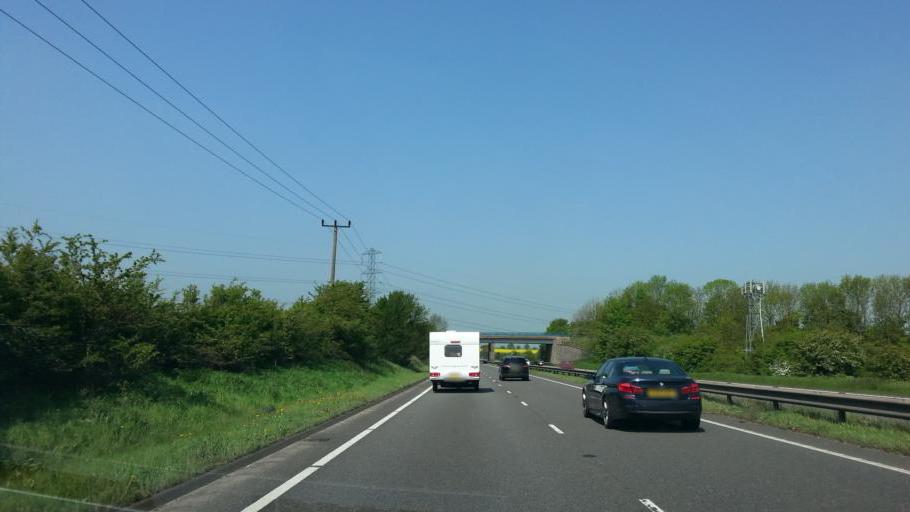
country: GB
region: England
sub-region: Nottinghamshire
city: South Collingham
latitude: 53.1828
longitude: -0.8229
